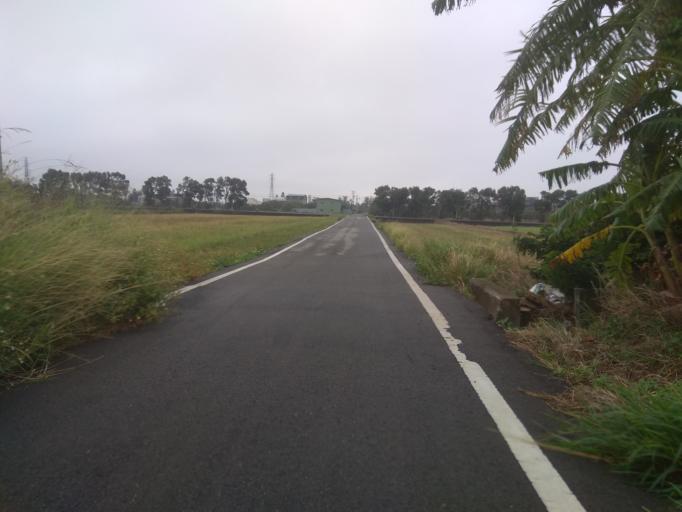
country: TW
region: Taiwan
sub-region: Hsinchu
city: Zhubei
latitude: 24.9915
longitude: 121.0343
